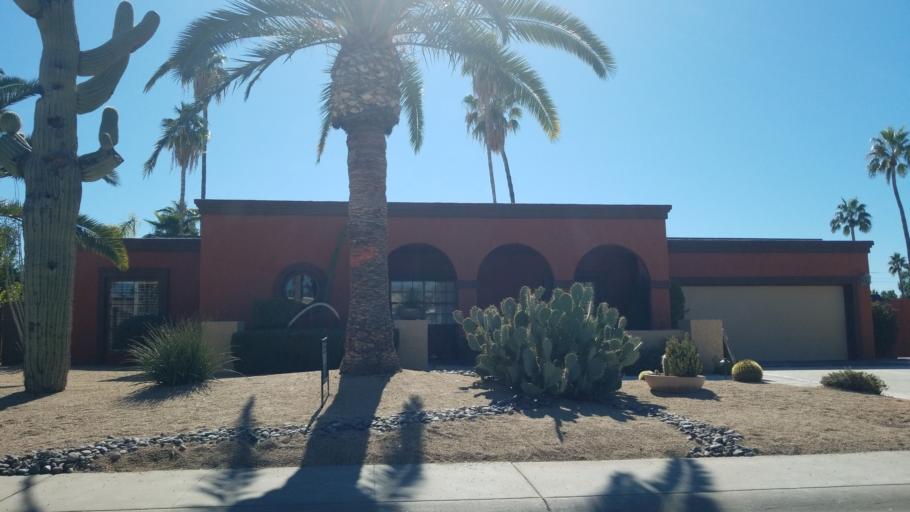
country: US
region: Arizona
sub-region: Maricopa County
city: Paradise Valley
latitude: 33.6120
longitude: -111.9292
